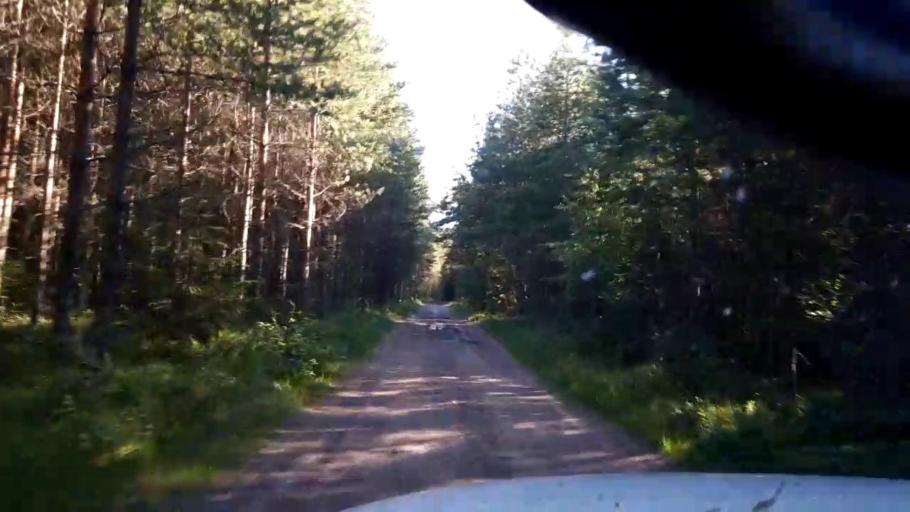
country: SE
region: Dalarna
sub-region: Borlange Kommun
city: Ornas
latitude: 60.3993
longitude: 15.5615
